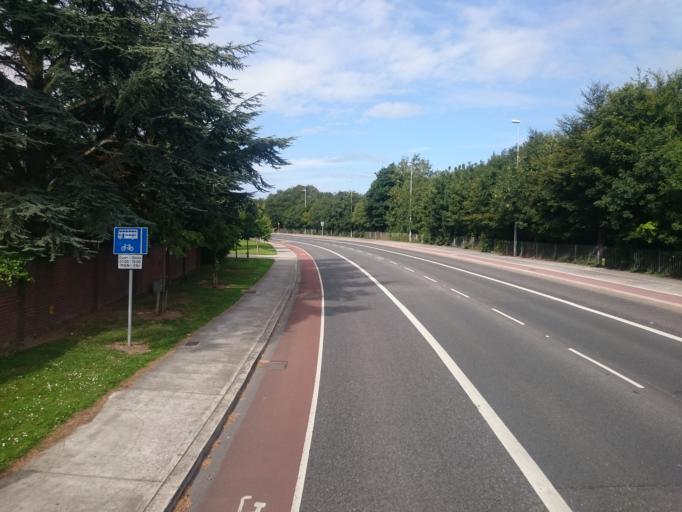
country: IE
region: Leinster
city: Ballyboden
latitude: 53.2893
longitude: -6.3213
